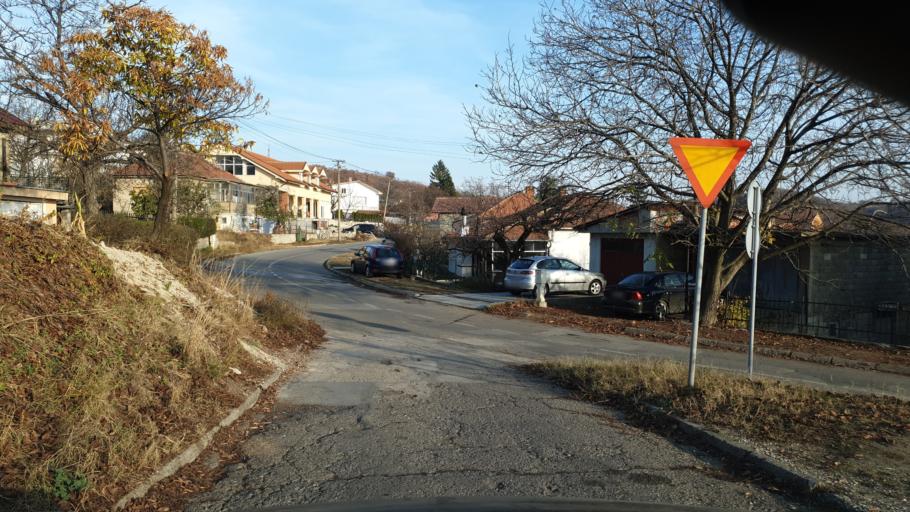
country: RS
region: Central Serbia
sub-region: Borski Okrug
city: Bor
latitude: 44.0504
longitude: 22.0975
